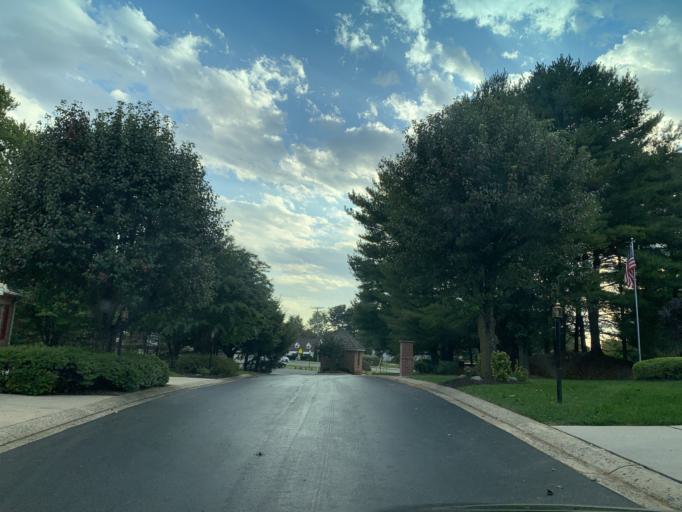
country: US
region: Maryland
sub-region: Harford County
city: Bel Air South
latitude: 39.5093
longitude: -76.3272
